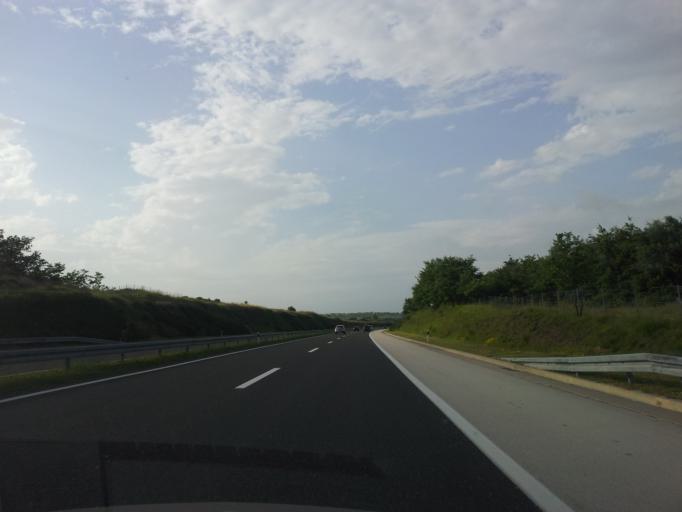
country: HR
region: Zadarska
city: Policnik
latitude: 44.1571
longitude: 15.4200
